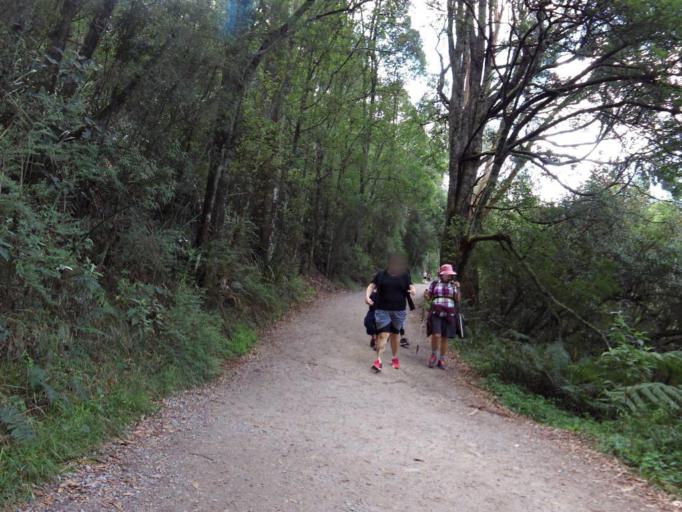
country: AU
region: Victoria
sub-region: Yarra Ranges
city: Ferny Creek
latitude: -37.8779
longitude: 145.3174
